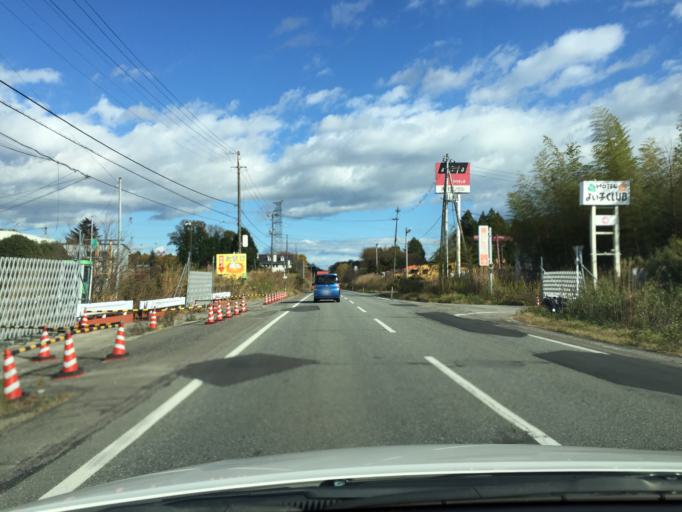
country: JP
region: Fukushima
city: Namie
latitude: 37.4217
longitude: 141.0029
